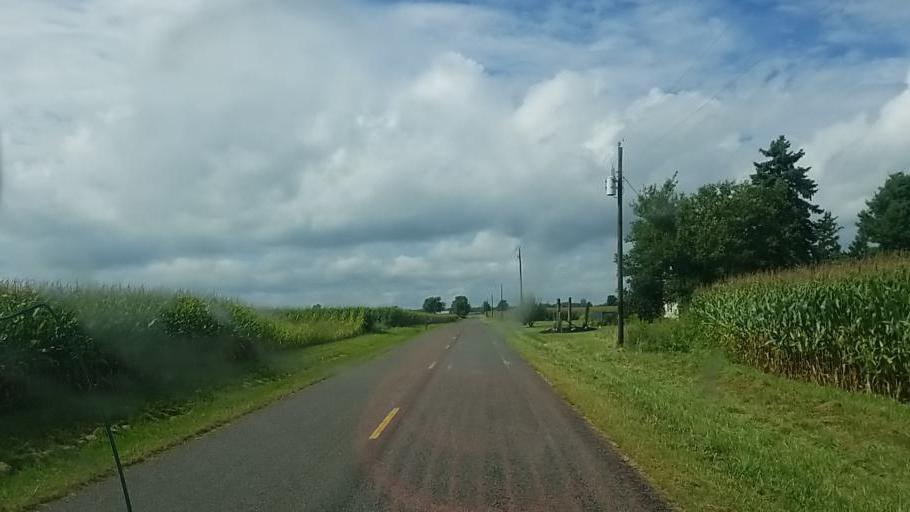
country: US
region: Ohio
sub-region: Hardin County
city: Kenton
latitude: 40.4852
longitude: -83.5145
